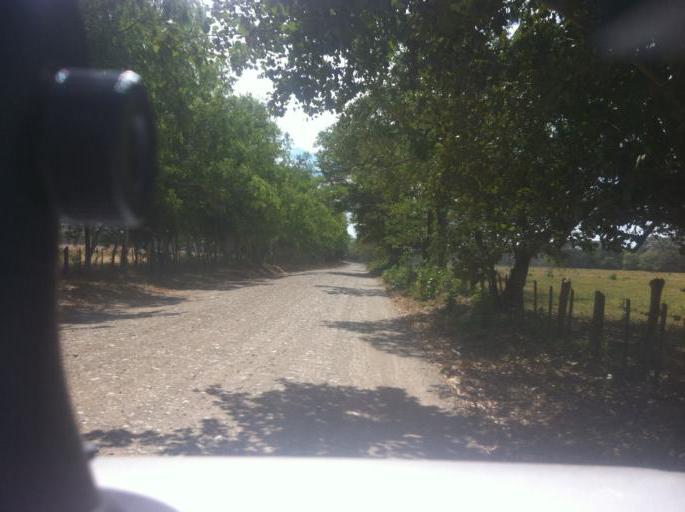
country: NI
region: Rivas
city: Tola
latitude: 11.5176
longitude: -86.0766
